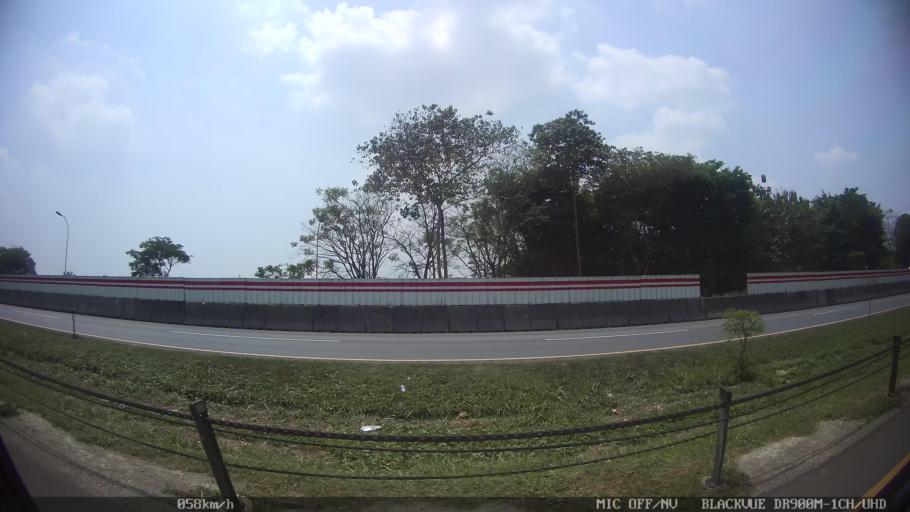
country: ID
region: West Java
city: Kresek
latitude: -6.1432
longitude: 106.2854
